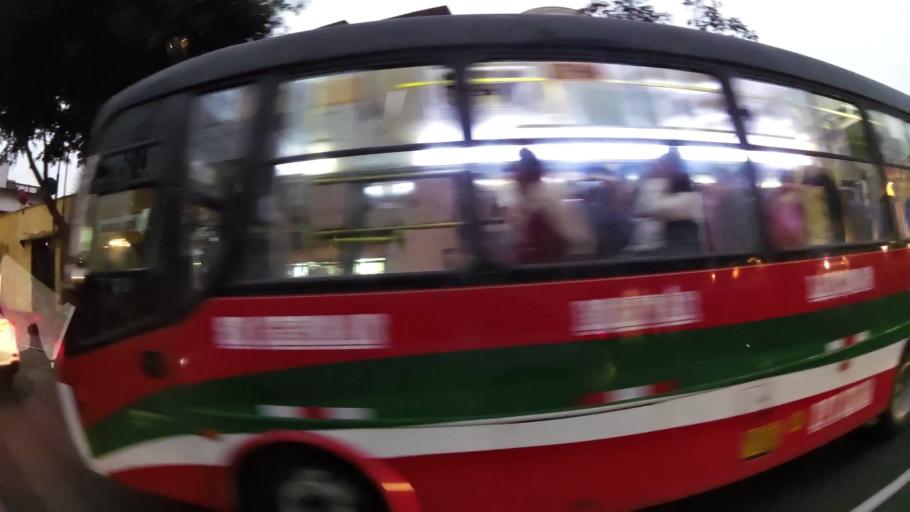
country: PE
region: Lima
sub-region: Lima
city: Surco
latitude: -12.1461
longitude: -77.0217
